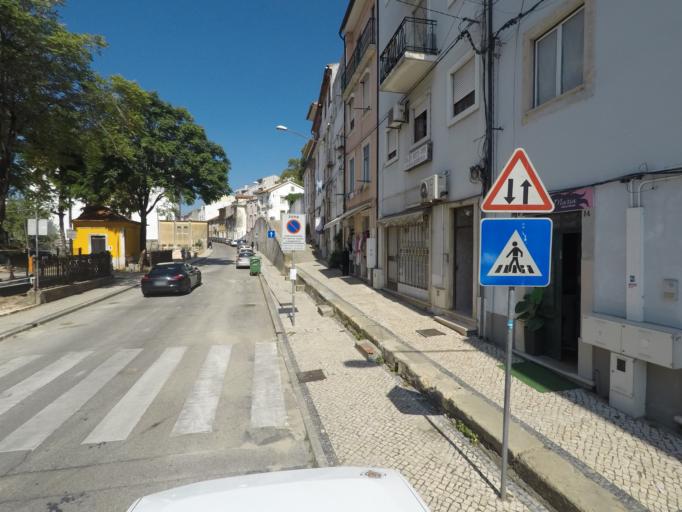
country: PT
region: Coimbra
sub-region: Coimbra
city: Coimbra
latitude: 40.2149
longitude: -8.4324
